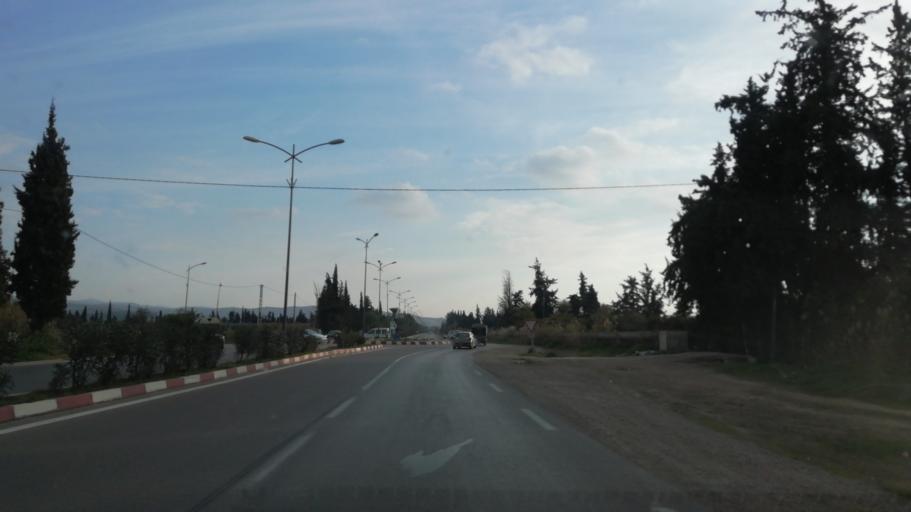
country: DZ
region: Mascara
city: Mascara
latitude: 35.6135
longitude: 0.0626
